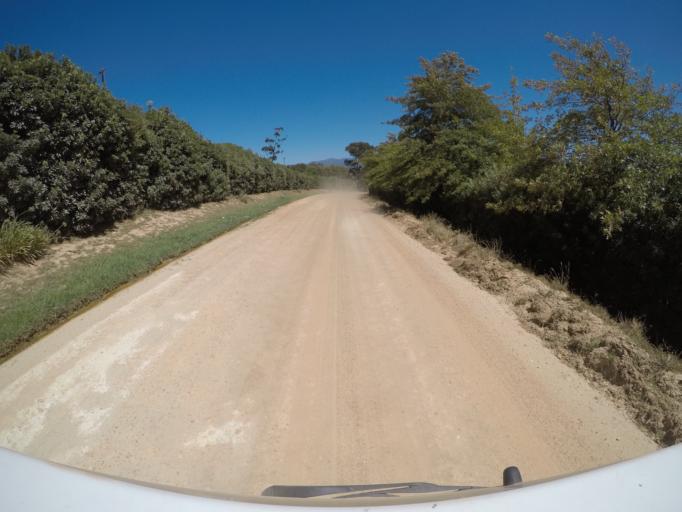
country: ZA
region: Western Cape
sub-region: Overberg District Municipality
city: Grabouw
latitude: -34.2453
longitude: 19.0986
